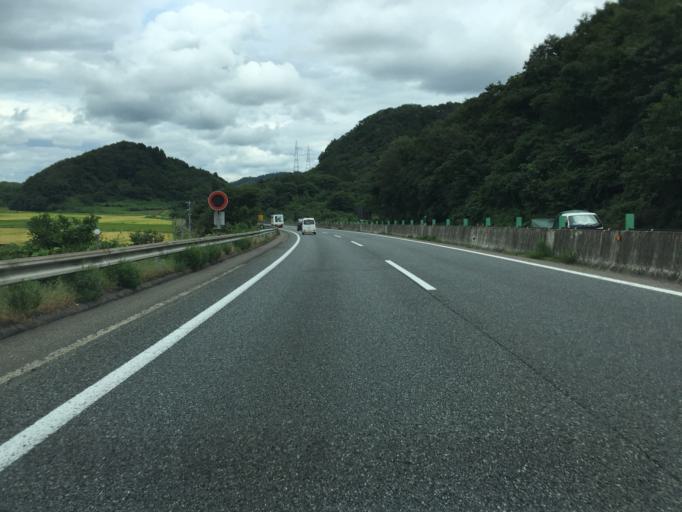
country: JP
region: Fukushima
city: Yanagawamachi-saiwaicho
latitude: 37.9140
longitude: 140.6011
